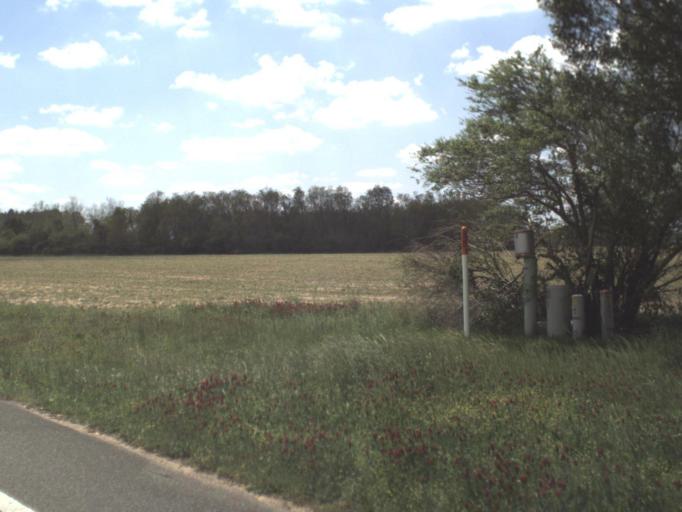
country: US
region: Florida
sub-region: Okaloosa County
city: Crestview
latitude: 30.8330
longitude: -86.6754
